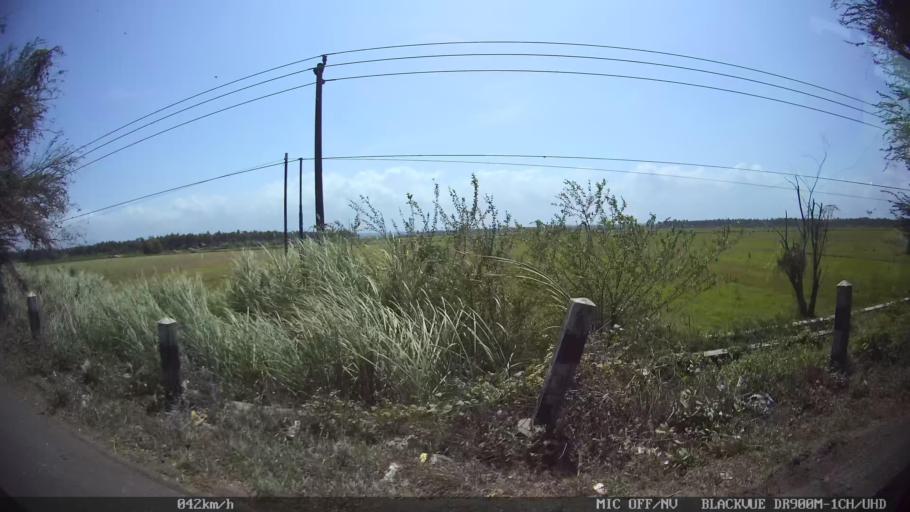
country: ID
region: Daerah Istimewa Yogyakarta
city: Srandakan
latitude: -7.9452
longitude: 110.1744
